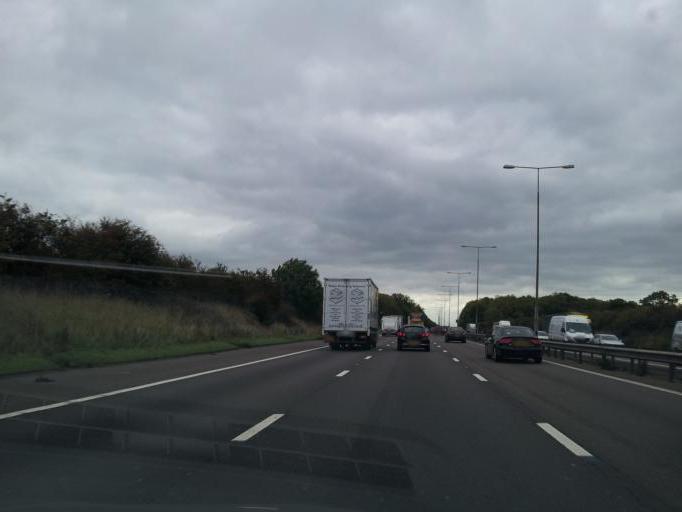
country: GB
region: England
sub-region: Northamptonshire
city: Hartwell
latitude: 52.1594
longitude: -0.8523
